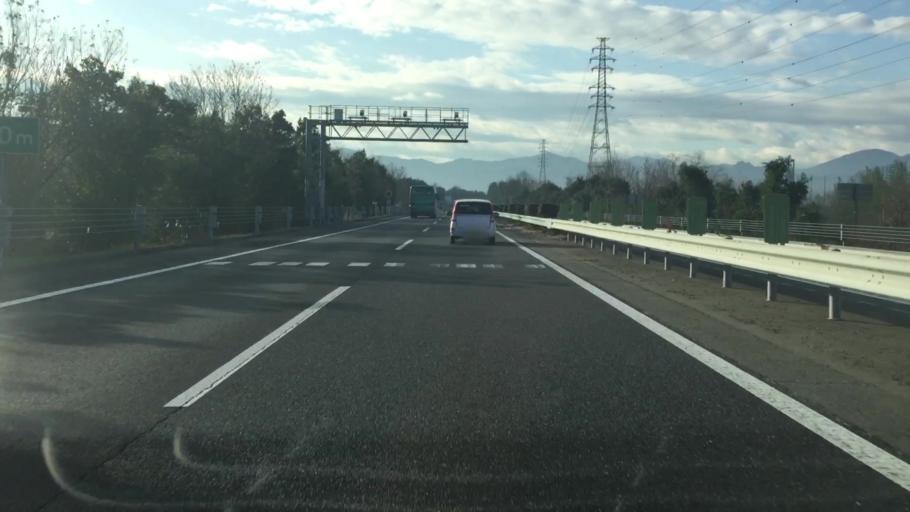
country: JP
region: Gunma
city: Fujioka
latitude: 36.2528
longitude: 139.0474
